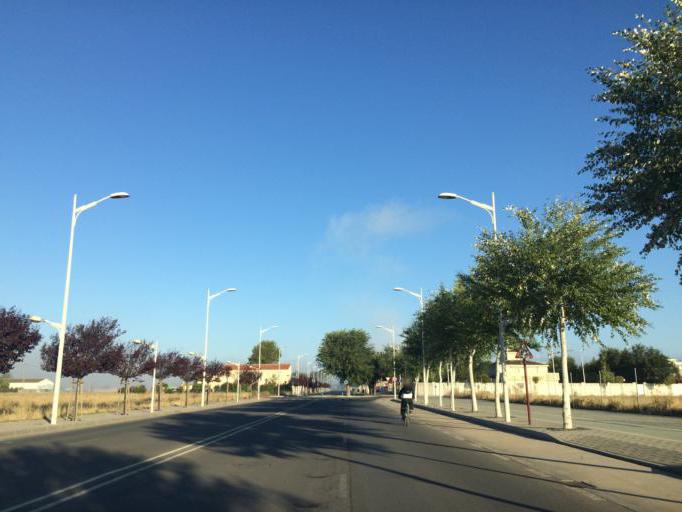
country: ES
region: Castille-La Mancha
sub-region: Provincia de Albacete
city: Albacete
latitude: 39.0018
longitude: -1.8788
